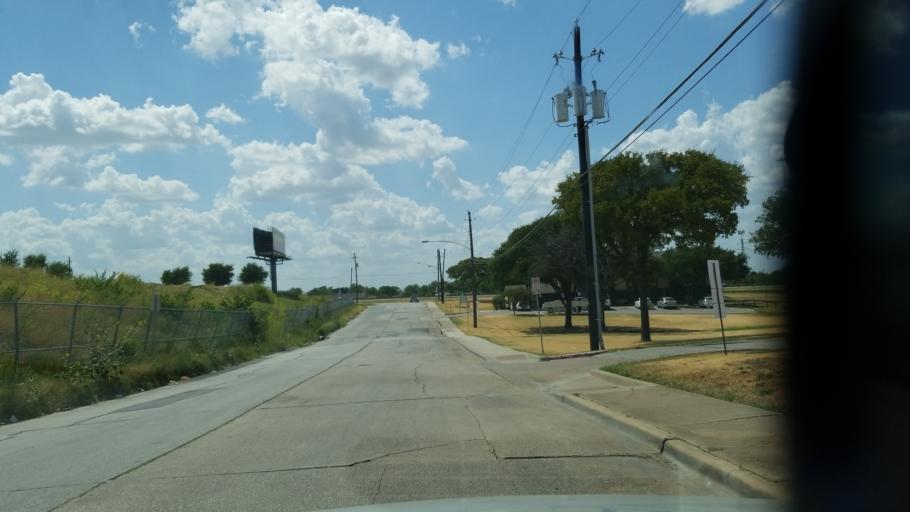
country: US
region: Texas
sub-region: Dallas County
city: Cockrell Hill
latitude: 32.7402
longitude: -96.9169
